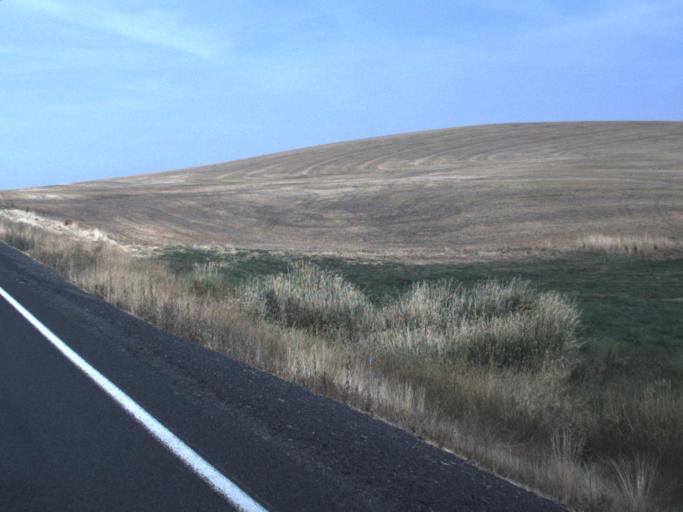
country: US
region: Idaho
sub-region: Benewah County
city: Plummer
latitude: 47.3037
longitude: -117.1639
